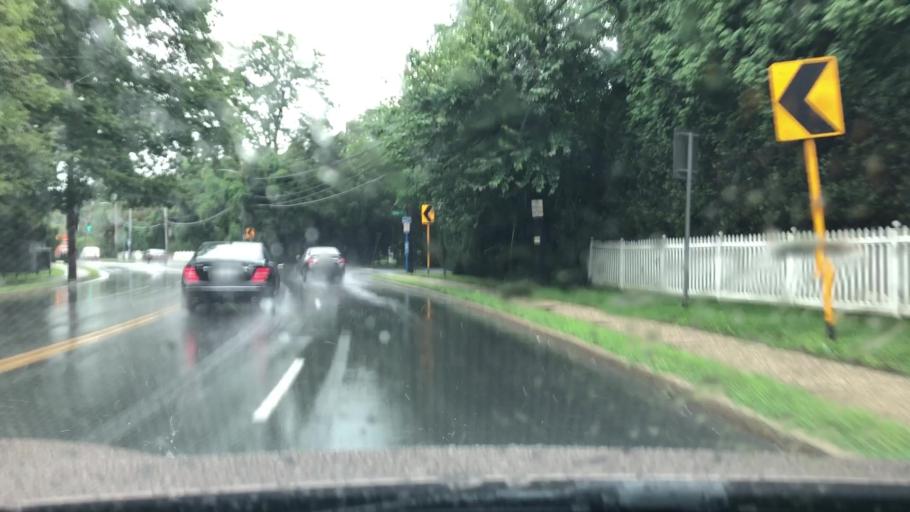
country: US
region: New York
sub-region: Westchester County
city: Tuckahoe
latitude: 40.9553
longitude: -73.8042
